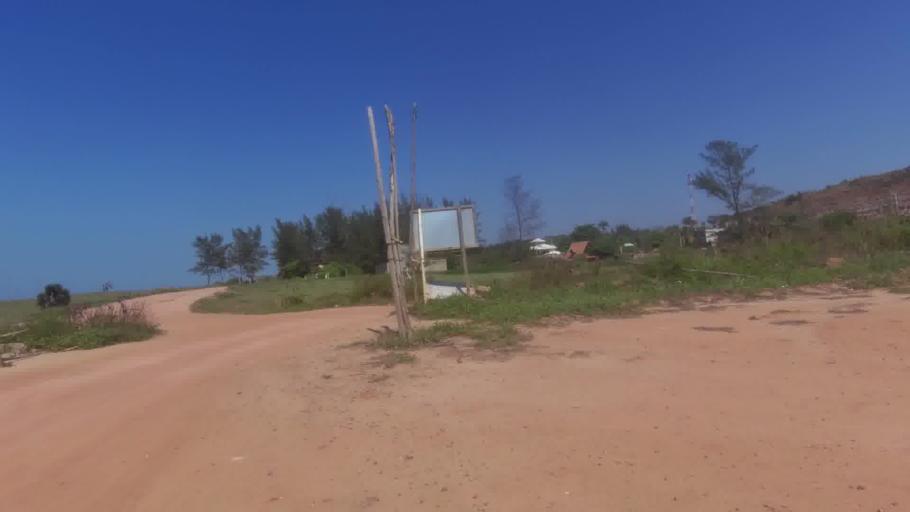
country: BR
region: Espirito Santo
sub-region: Marataizes
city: Marataizes
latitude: -21.1111
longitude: -40.8538
